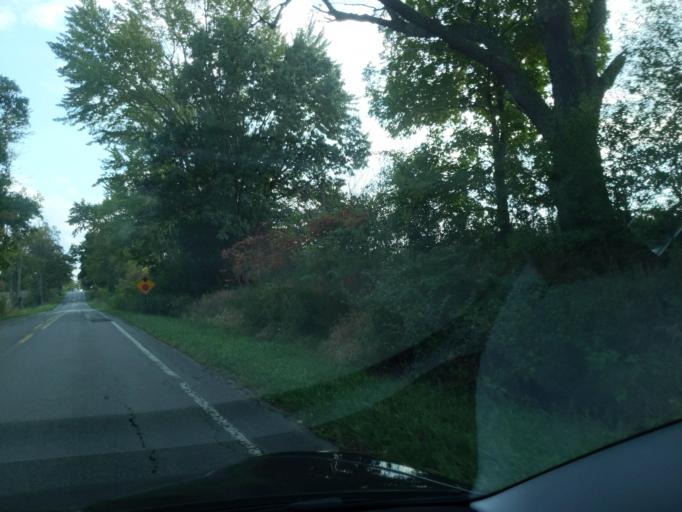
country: US
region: Michigan
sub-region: Jackson County
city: Jackson
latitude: 42.2793
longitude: -84.4832
